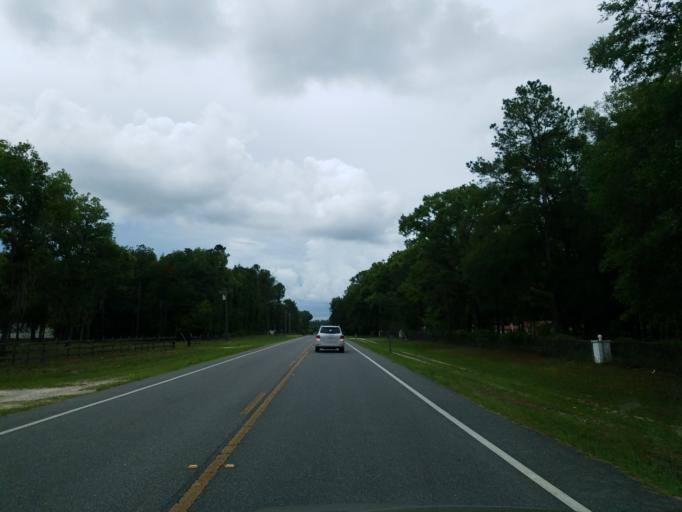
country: US
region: Florida
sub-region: Alachua County
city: High Springs
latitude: 29.9081
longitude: -82.5016
